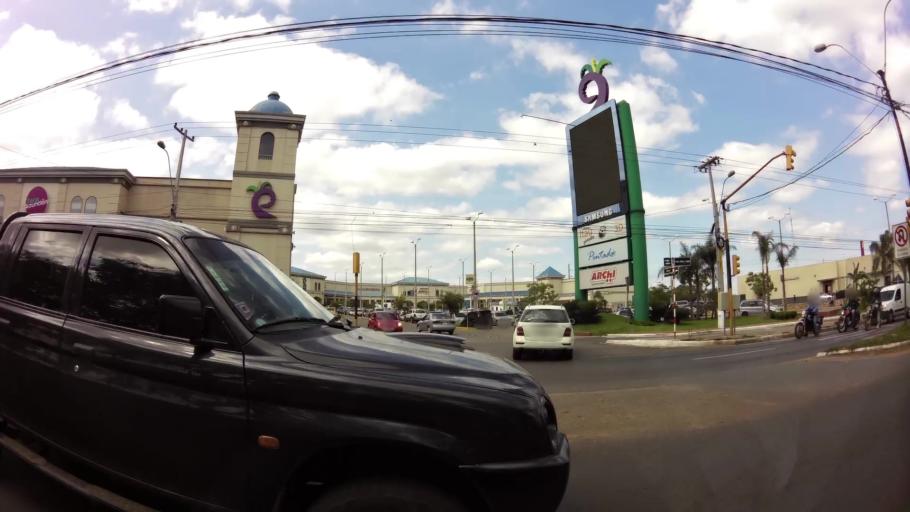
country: PY
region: Central
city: Fernando de la Mora
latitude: -25.3243
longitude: -57.5210
